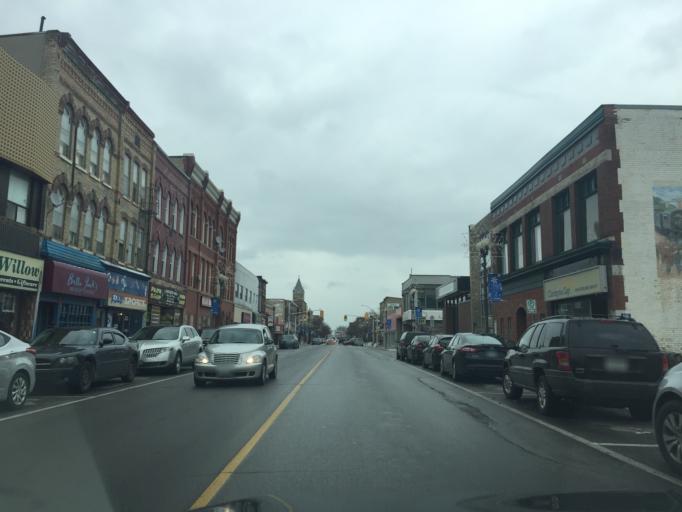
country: CA
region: Ontario
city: St. Thomas
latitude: 42.7790
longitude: -81.1962
